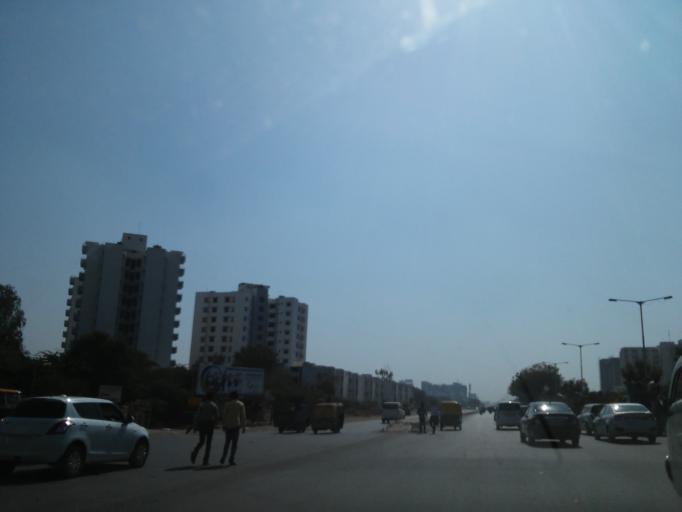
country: IN
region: Gujarat
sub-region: Ahmadabad
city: Ahmedabad
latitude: 23.0882
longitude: 72.5287
